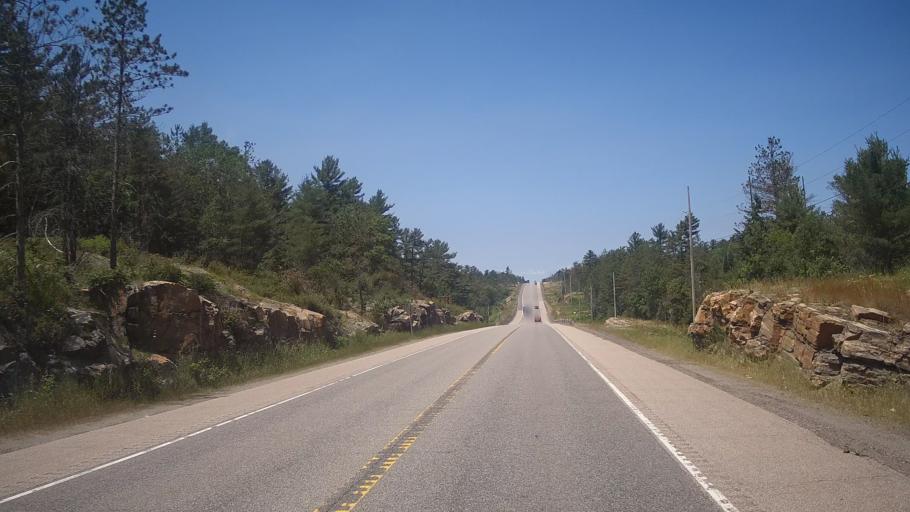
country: CA
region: Ontario
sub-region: Parry Sound District
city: Parry Sound
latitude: 45.6525
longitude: -80.4047
